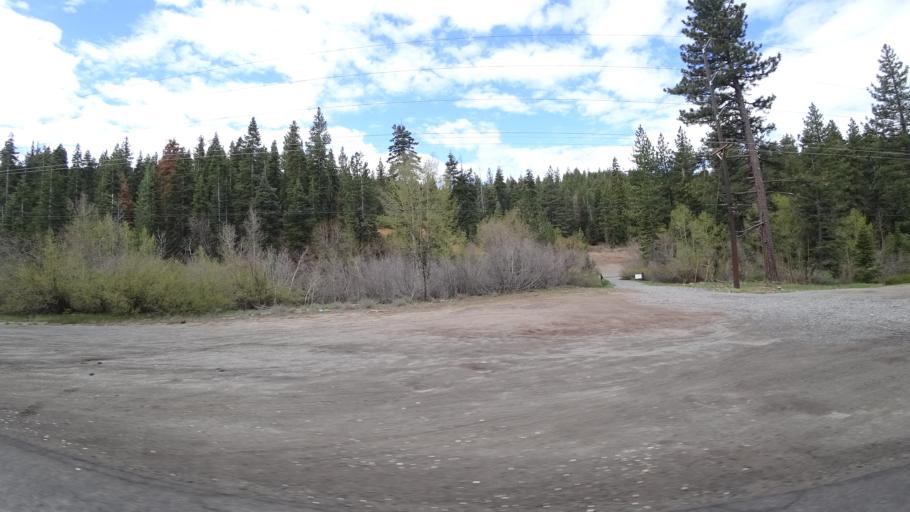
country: US
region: California
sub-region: Placer County
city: Tahoe Vista
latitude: 39.2756
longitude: -120.1019
